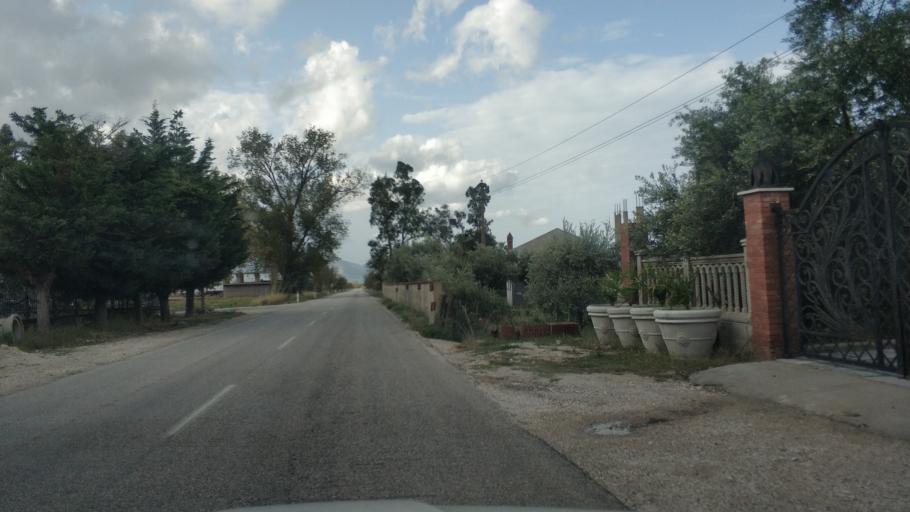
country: AL
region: Vlore
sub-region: Rrethi i Vlores
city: Orikum
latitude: 40.2835
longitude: 19.4991
